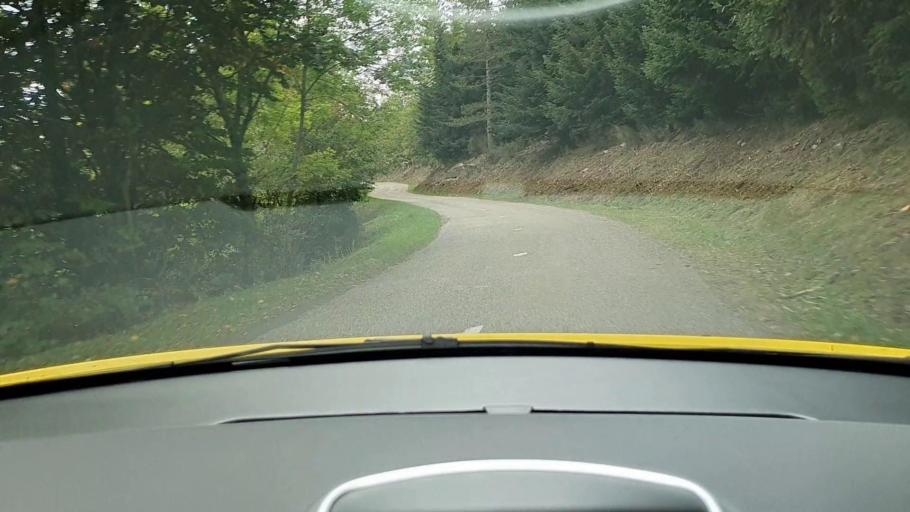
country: FR
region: Languedoc-Roussillon
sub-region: Departement de la Lozere
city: Meyrueis
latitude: 44.0974
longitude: 3.4701
